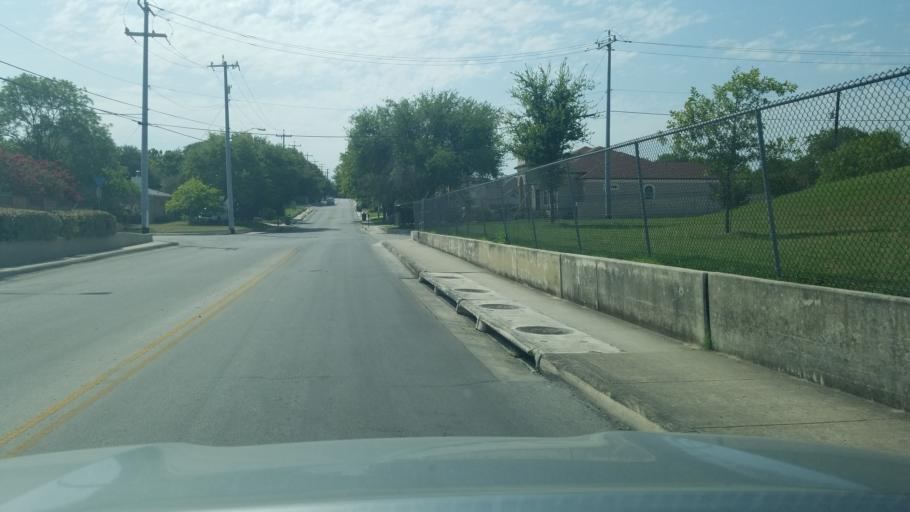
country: US
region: Texas
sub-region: Bexar County
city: Castle Hills
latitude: 29.5435
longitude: -98.5206
